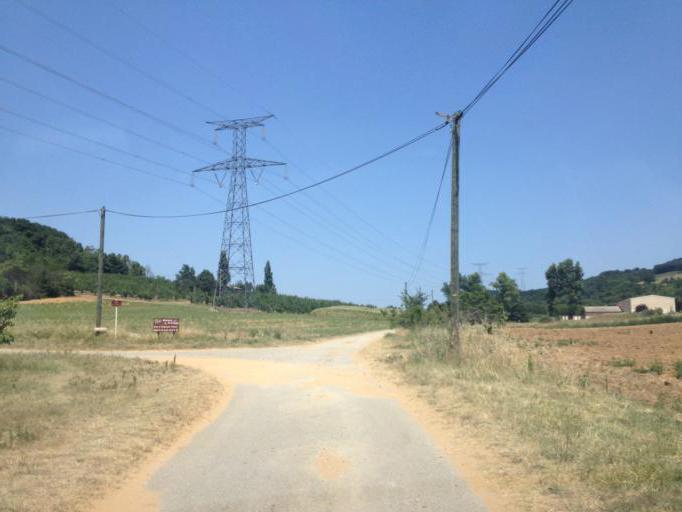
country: FR
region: Rhone-Alpes
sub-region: Departement de la Drome
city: Clerieux
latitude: 45.1354
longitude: 4.9403
